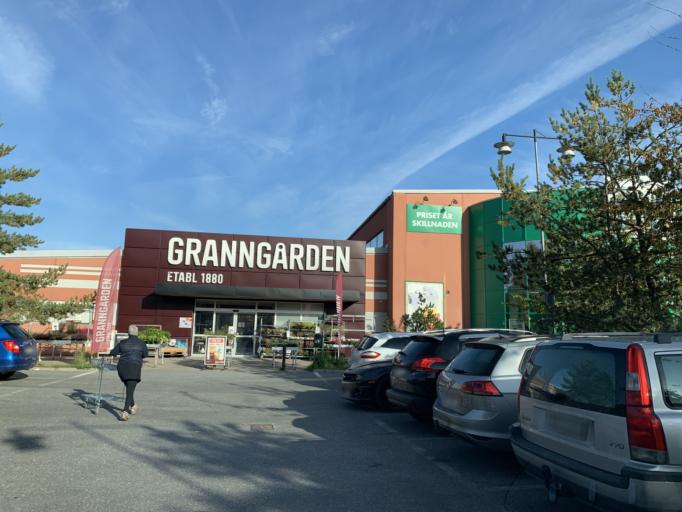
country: SE
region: Stockholm
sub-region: Haninge Kommun
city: Haninge
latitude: 59.1760
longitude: 18.1437
